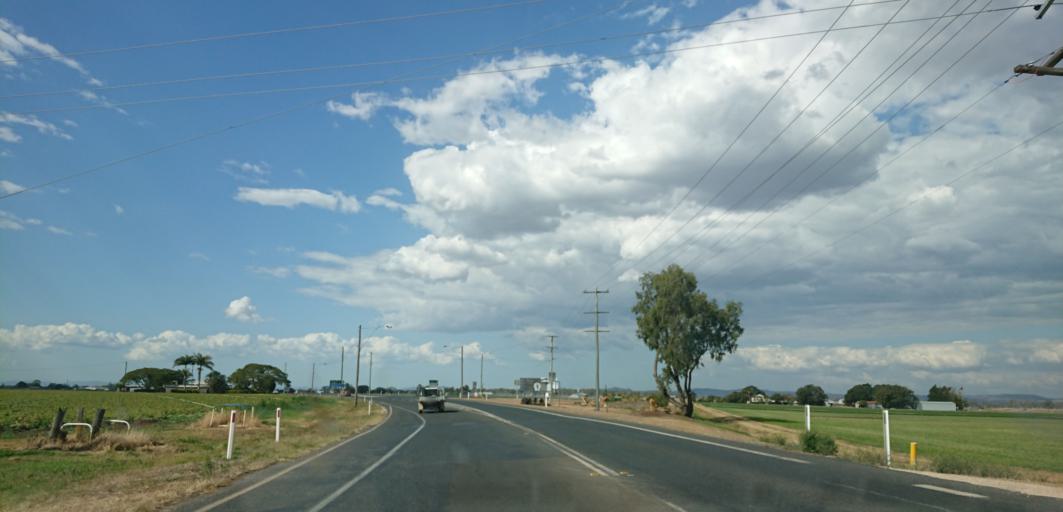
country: AU
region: Queensland
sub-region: Lockyer Valley
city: Gatton
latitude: -27.5548
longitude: 152.3039
